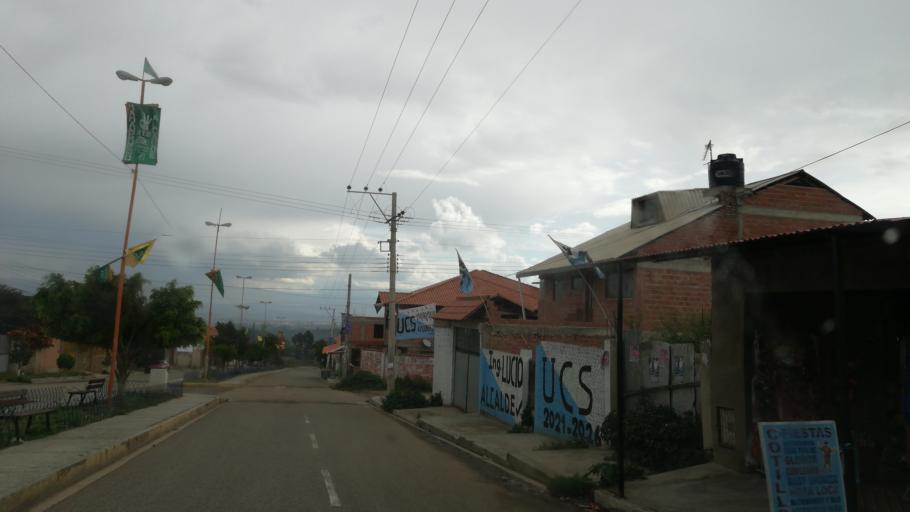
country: BO
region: Cochabamba
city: Cochabamba
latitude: -17.3349
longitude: -66.1980
